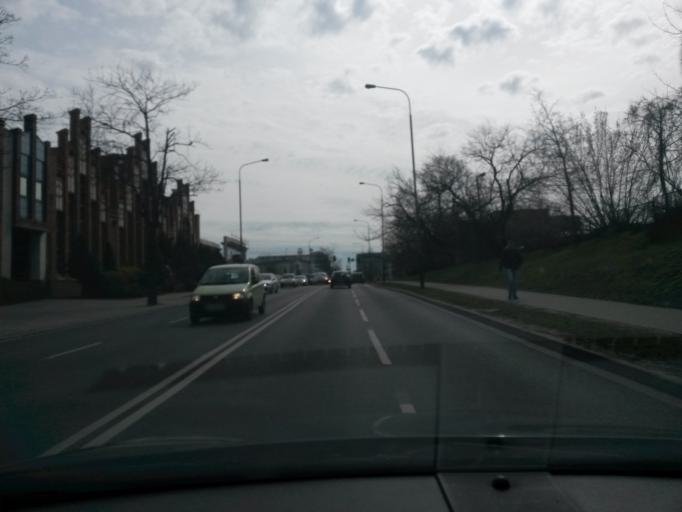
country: PL
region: Greater Poland Voivodeship
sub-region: Poznan
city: Poznan
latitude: 52.4157
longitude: 16.9394
